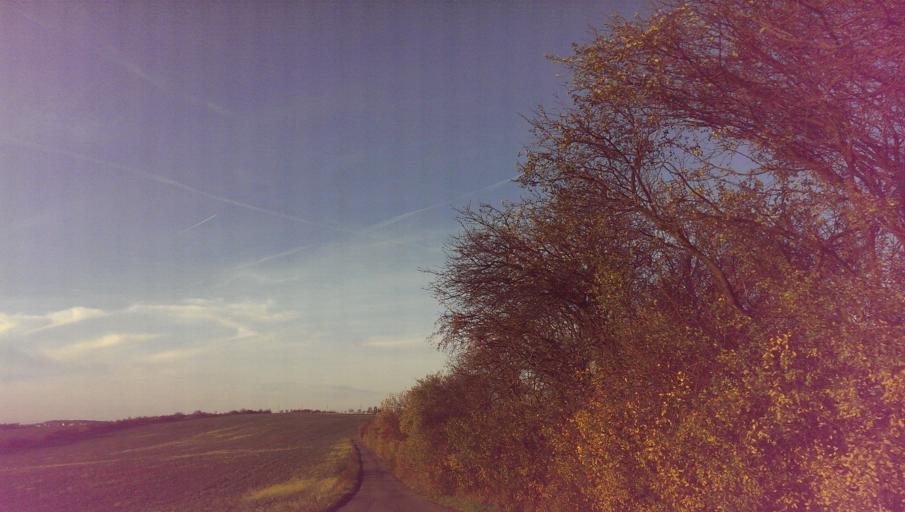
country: CZ
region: Zlin
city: Brezolupy
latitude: 49.1600
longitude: 17.6030
